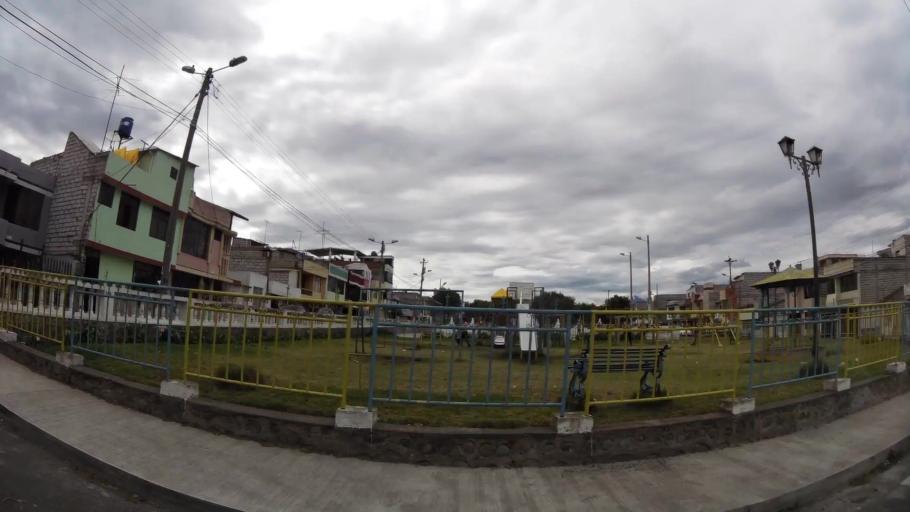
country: EC
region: Cotopaxi
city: Latacunga
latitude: -0.9353
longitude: -78.6222
